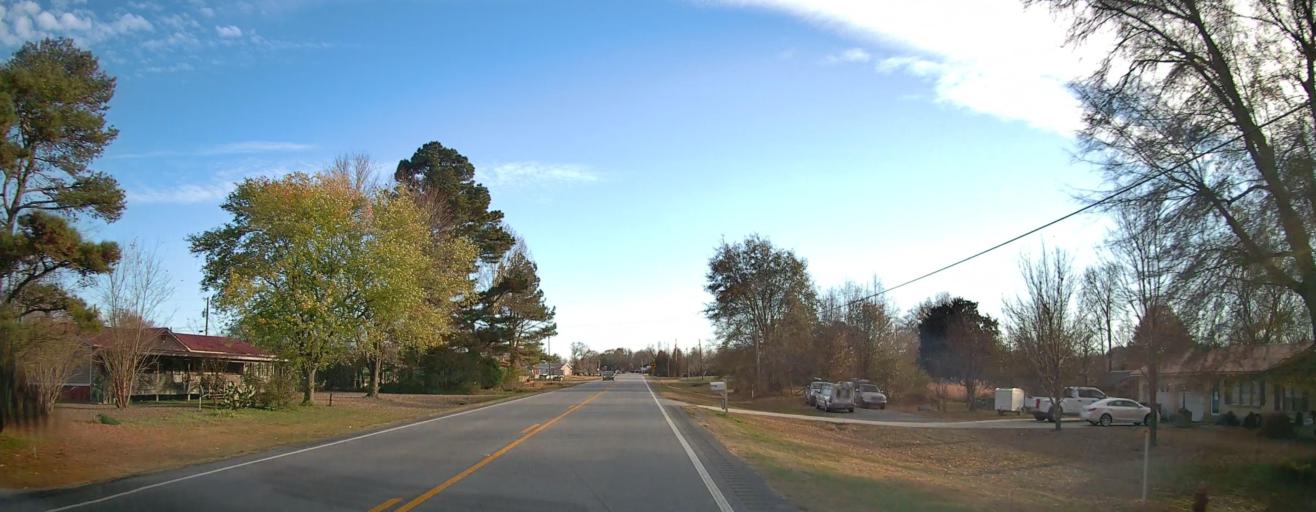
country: US
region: Alabama
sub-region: Marshall County
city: Arab
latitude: 34.3161
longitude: -86.6007
